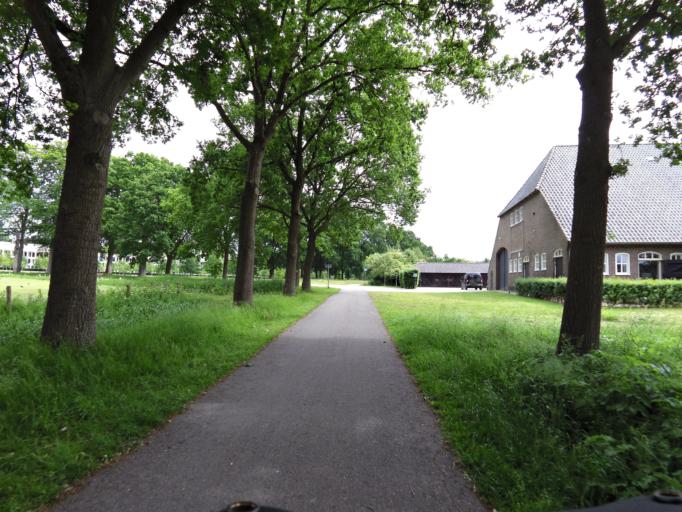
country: NL
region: North Brabant
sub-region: Gemeente Breda
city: Breda
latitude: 51.5595
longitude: 4.7851
